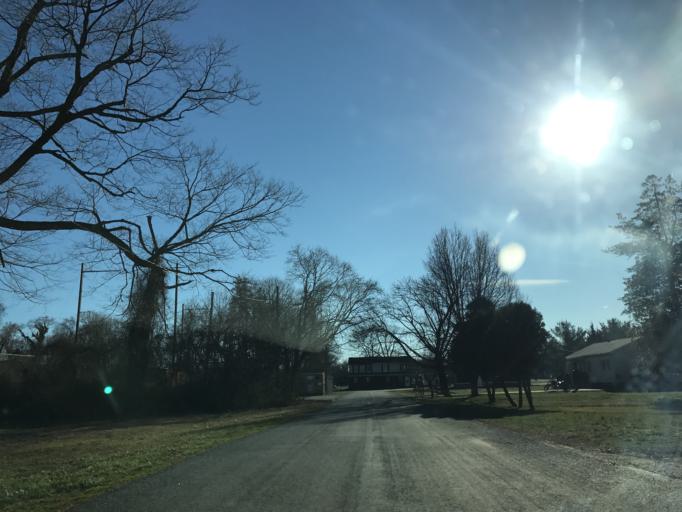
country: US
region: Maryland
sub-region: Harford County
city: Perryman
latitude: 39.4668
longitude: -76.2000
